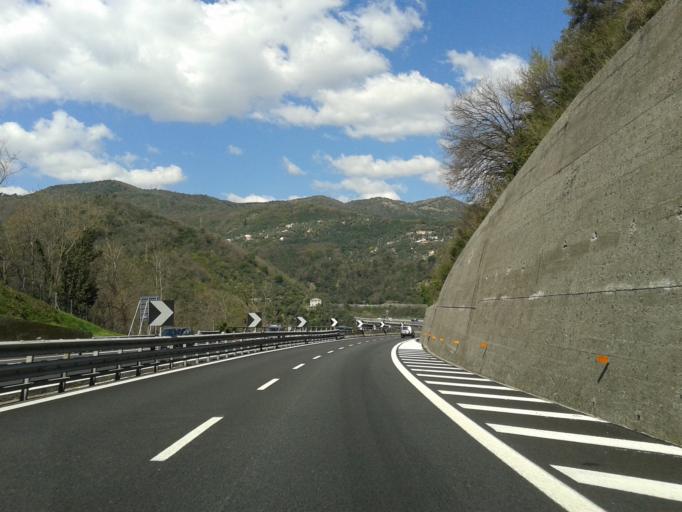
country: IT
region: Liguria
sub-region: Provincia di Genova
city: Avegno
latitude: 44.3703
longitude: 9.1545
